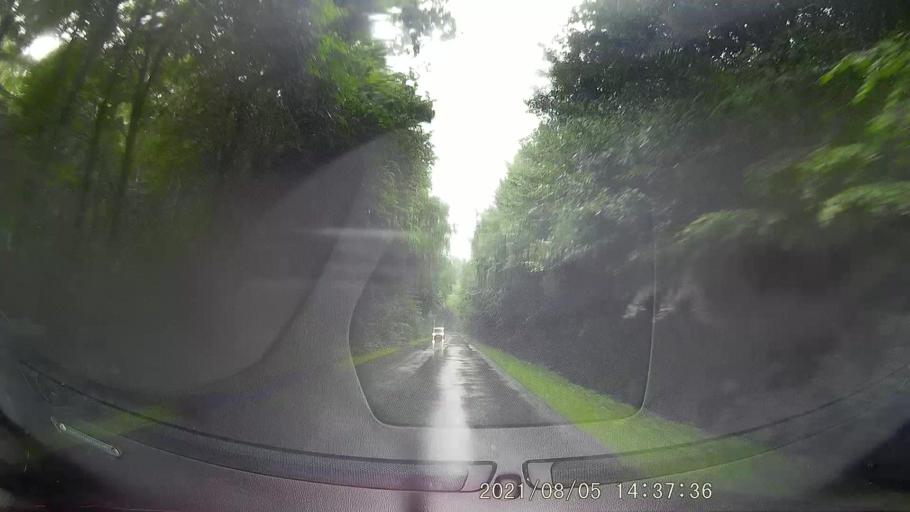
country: PL
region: Opole Voivodeship
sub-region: Powiat nyski
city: Sidzina
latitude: 50.4683
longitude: 17.4717
